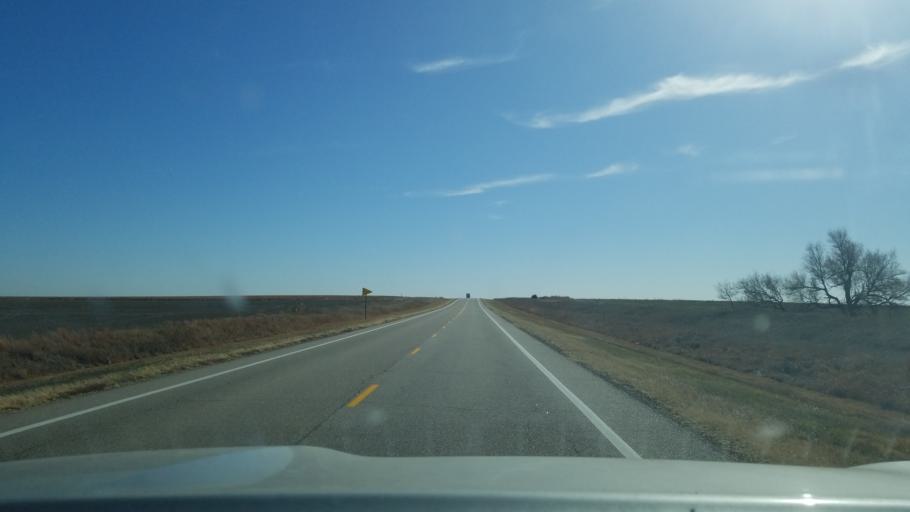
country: US
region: Kansas
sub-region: Ford County
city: Dodge City
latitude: 37.5813
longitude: -99.6769
